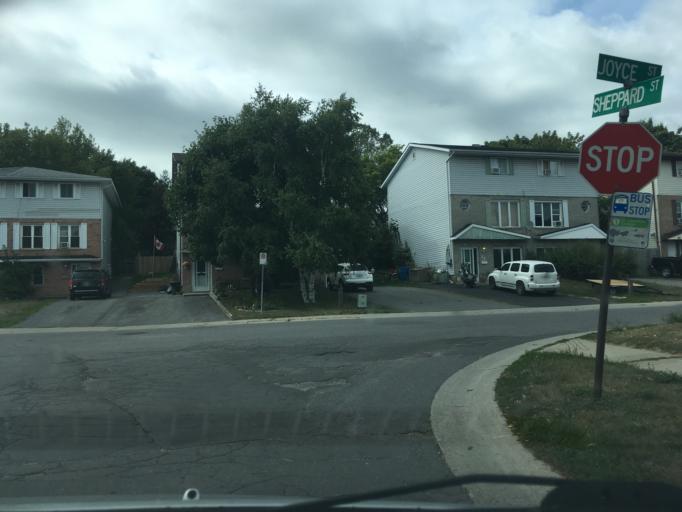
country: CA
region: Ontario
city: Kingston
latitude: 44.2736
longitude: -76.4782
